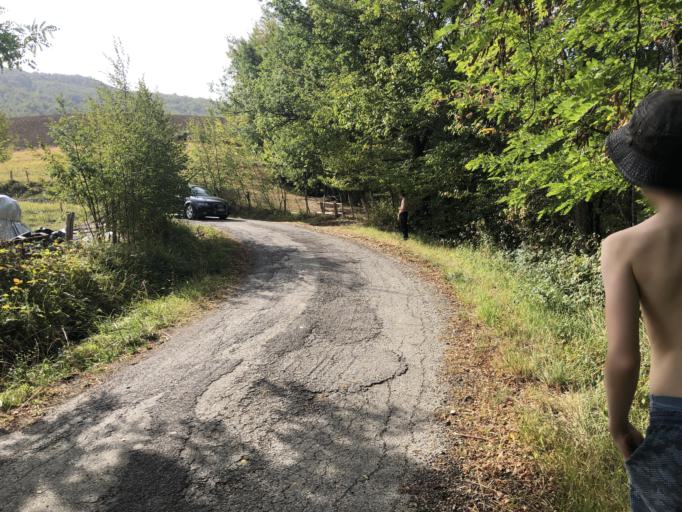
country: IT
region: Emilia-Romagna
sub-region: Forli-Cesena
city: Portico e San Benedetto
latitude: 44.0211
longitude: 11.7874
